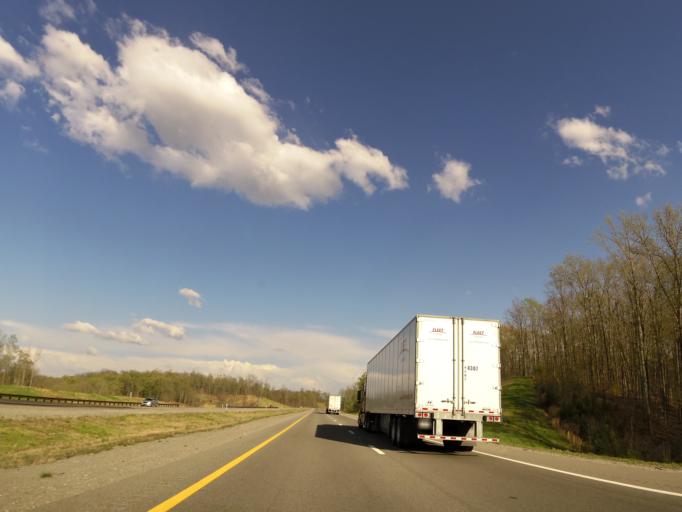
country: US
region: Tennessee
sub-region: Williamson County
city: Thompson's Station
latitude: 35.8243
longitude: -87.0491
